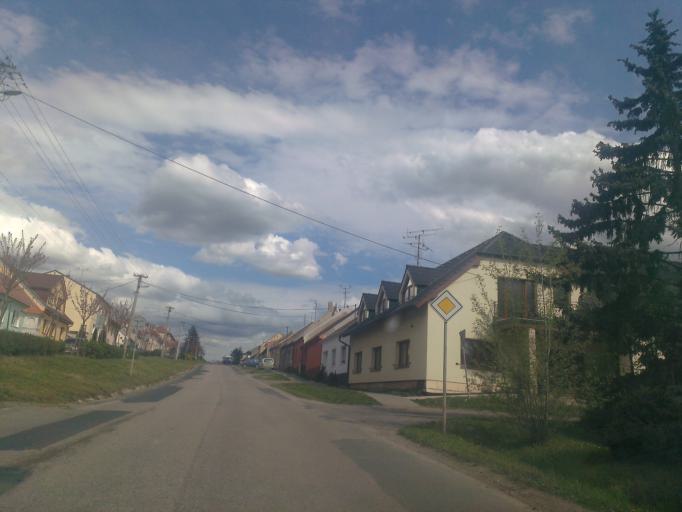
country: CZ
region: South Moravian
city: Zelesice
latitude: 49.1174
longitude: 16.5863
